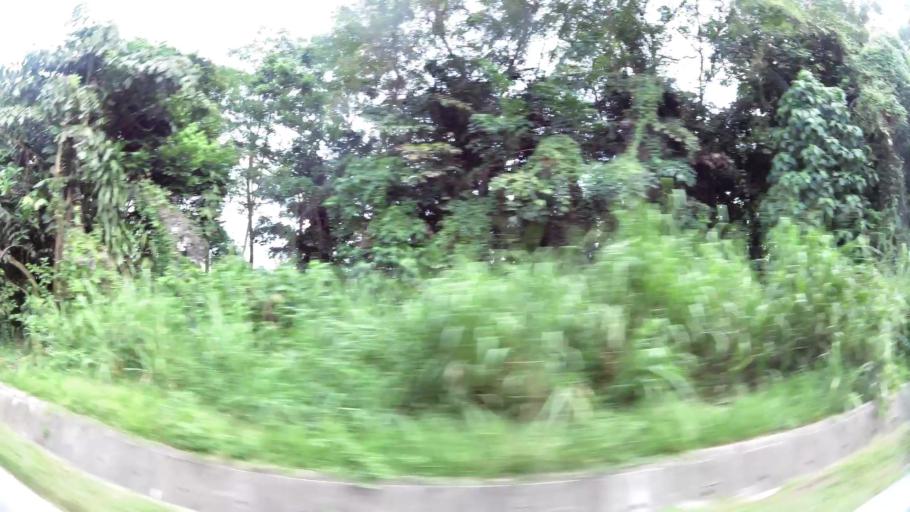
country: MY
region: Johor
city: Johor Bahru
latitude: 1.4361
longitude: 103.7260
